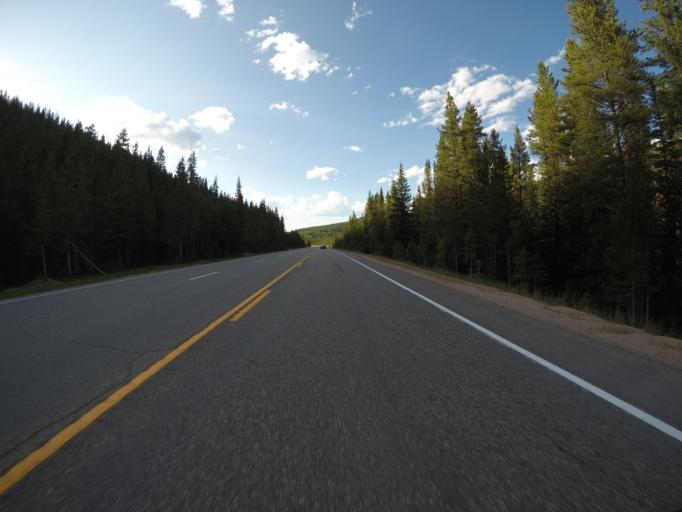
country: US
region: Colorado
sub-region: Grand County
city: Fraser
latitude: 39.8736
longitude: -105.7512
